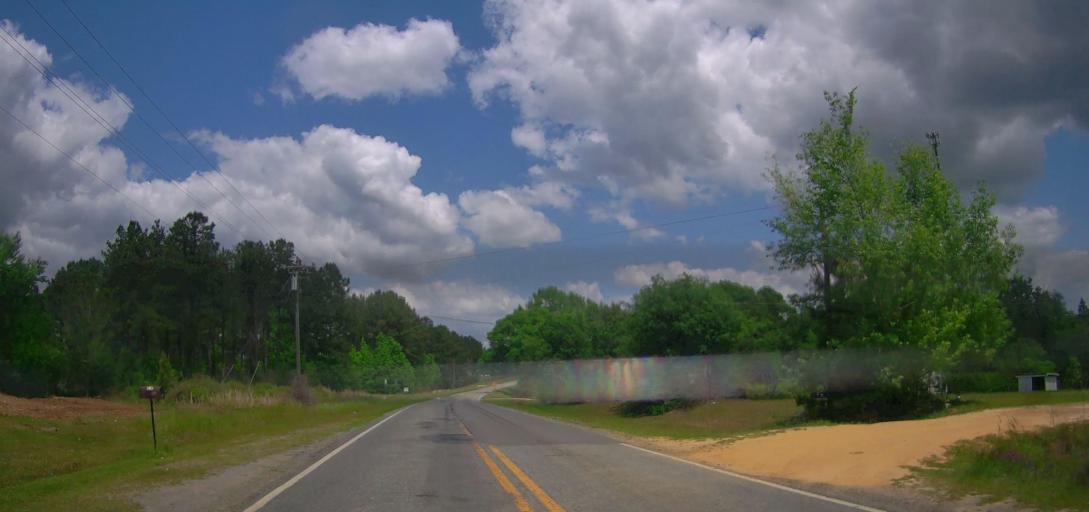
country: US
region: Georgia
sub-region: Laurens County
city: East Dublin
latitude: 32.5760
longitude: -82.7970
